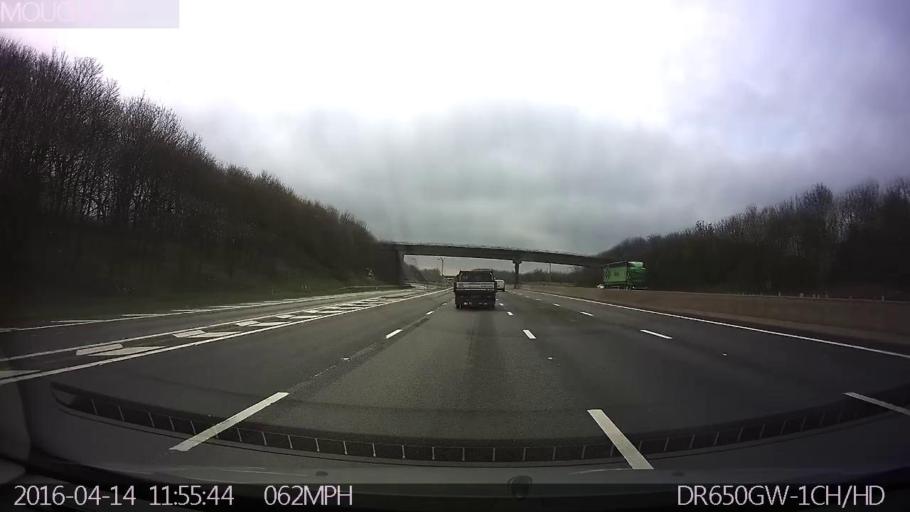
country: GB
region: England
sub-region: Derbyshire
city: Tibshelf
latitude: 53.1406
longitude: -1.3309
